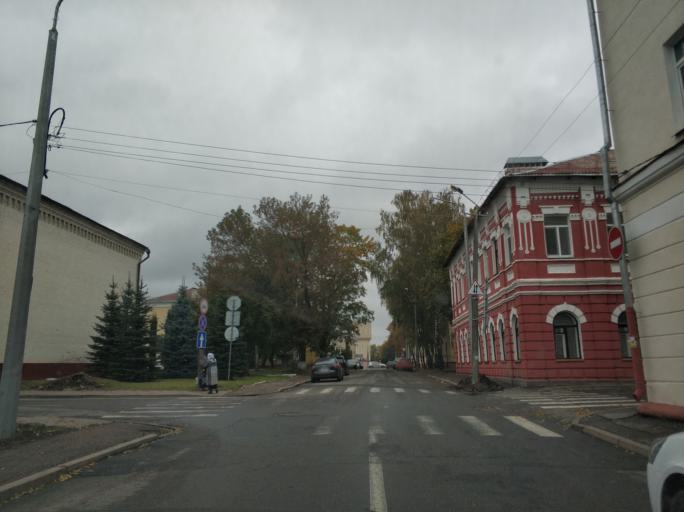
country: BY
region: Vitebsk
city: Polatsk
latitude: 55.4857
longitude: 28.7709
